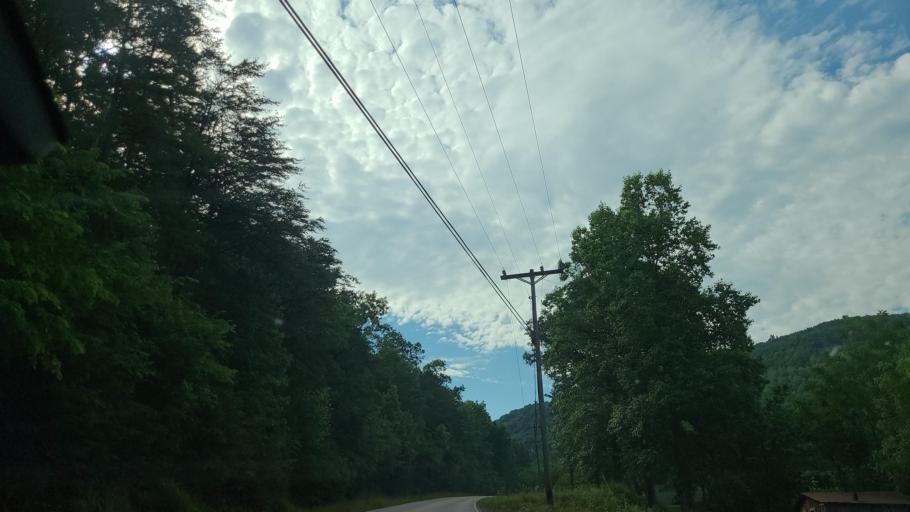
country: US
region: Kentucky
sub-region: Knox County
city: Barbourville
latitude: 36.6807
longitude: -83.9491
